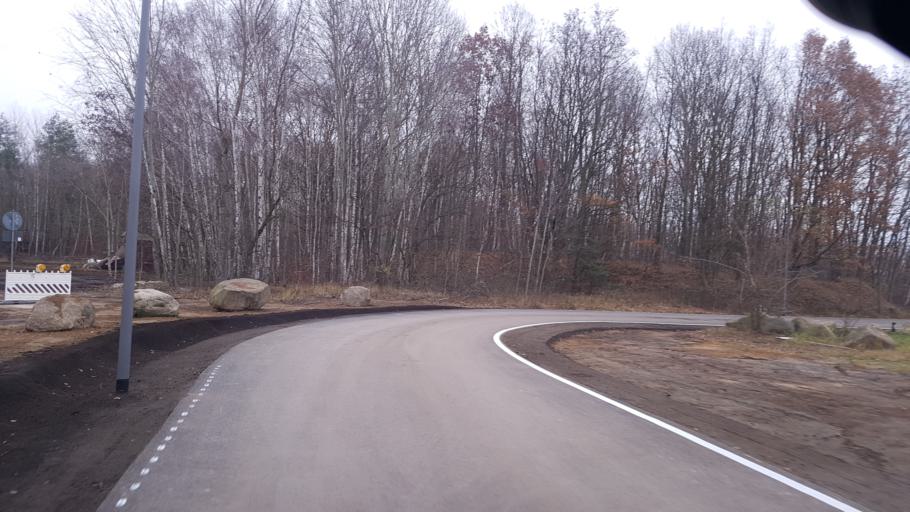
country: DE
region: Brandenburg
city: Sallgast
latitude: 51.5888
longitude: 13.7857
